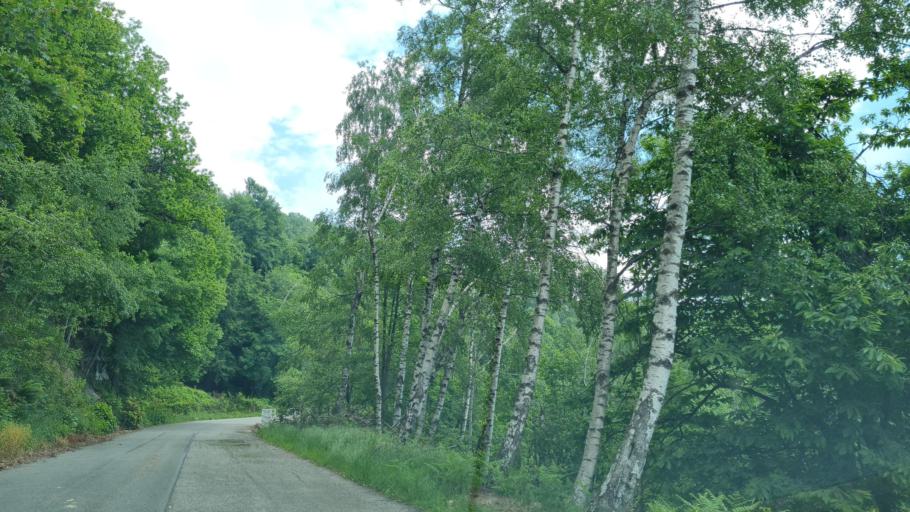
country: IT
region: Piedmont
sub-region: Provincia di Biella
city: Sordevolo
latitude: 45.5918
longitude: 7.9657
